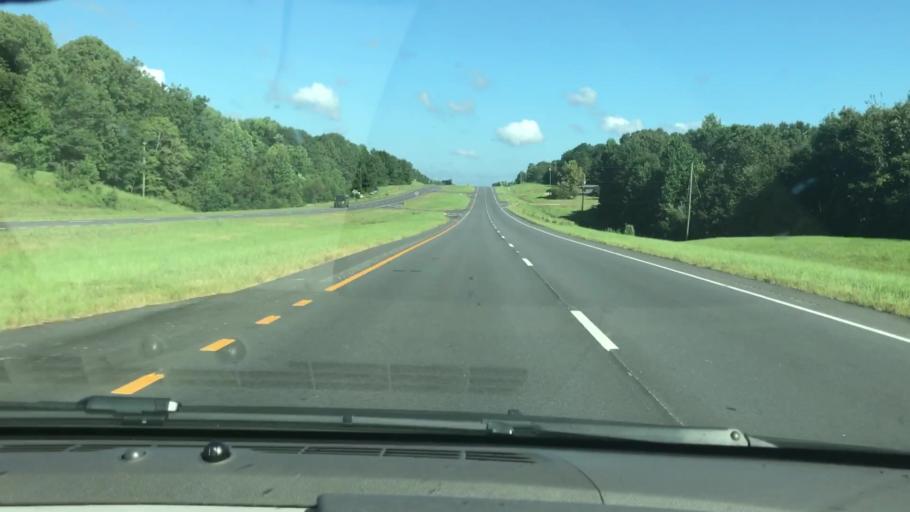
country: US
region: Alabama
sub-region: Barbour County
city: Eufaula
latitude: 32.0336
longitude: -85.1236
